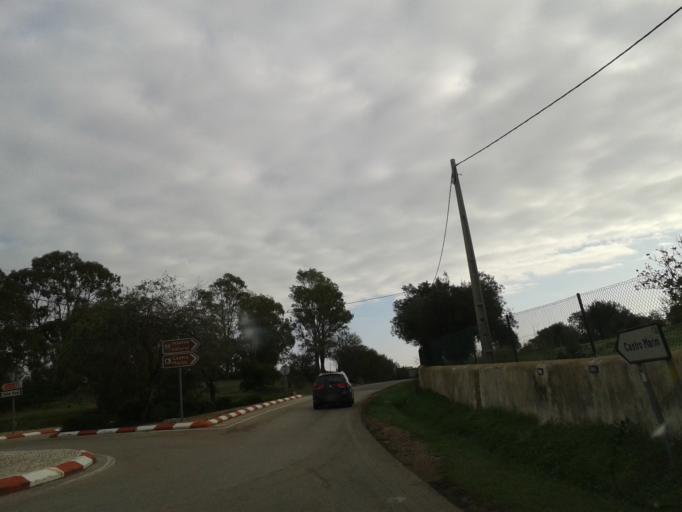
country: PT
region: Faro
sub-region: Castro Marim
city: Castro Marim
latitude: 37.2186
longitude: -7.4616
